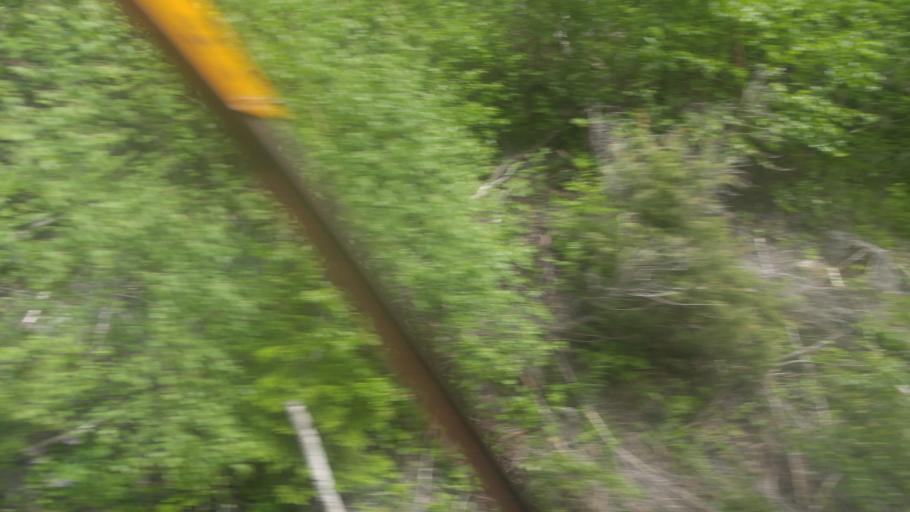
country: NO
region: Sor-Trondelag
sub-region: Selbu
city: Mebonden
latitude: 62.9665
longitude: 10.9589
